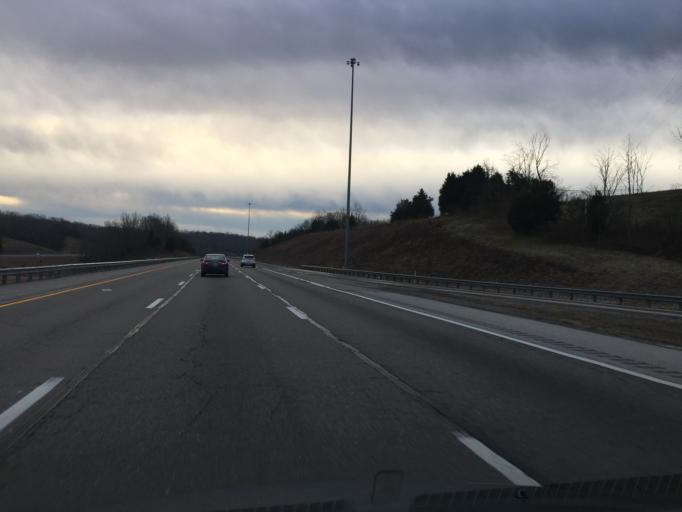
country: US
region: Kentucky
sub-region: Grant County
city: Williamstown
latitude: 38.4874
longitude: -84.5854
